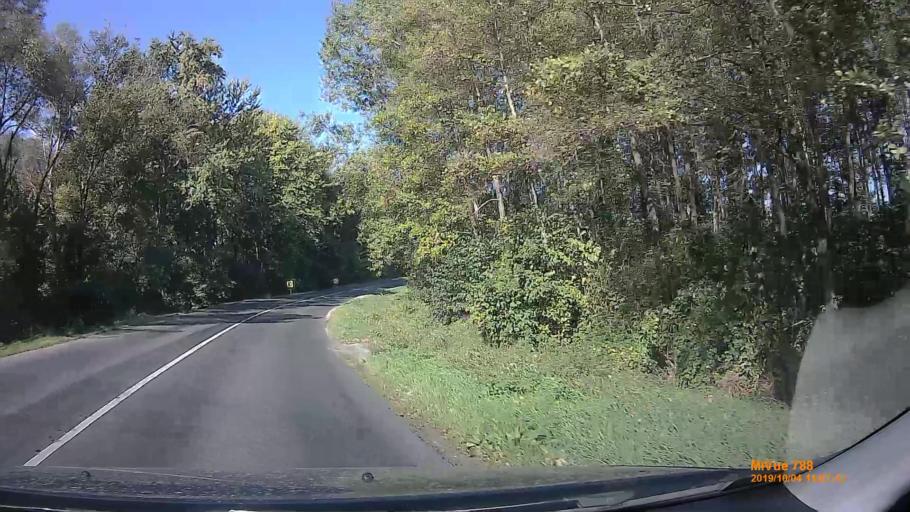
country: HU
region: Somogy
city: Kaposmero
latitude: 46.4000
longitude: 17.7416
